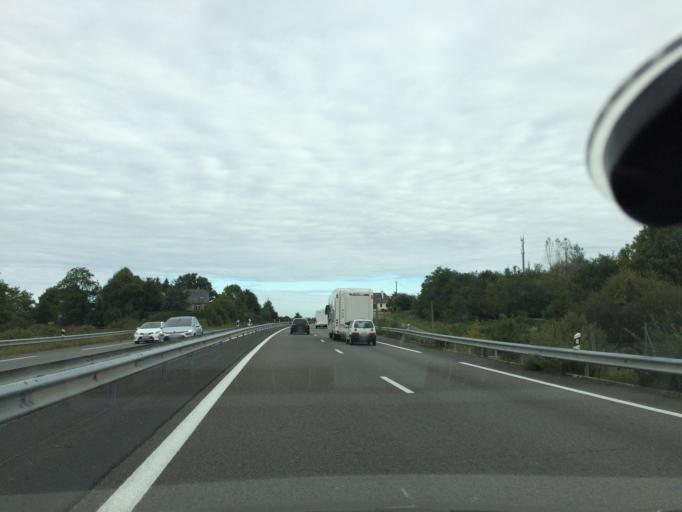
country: FR
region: Brittany
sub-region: Departement d'Ille-et-Vilaine
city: Saint-Pierre-de-Plesguen
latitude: 48.4422
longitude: -1.9248
